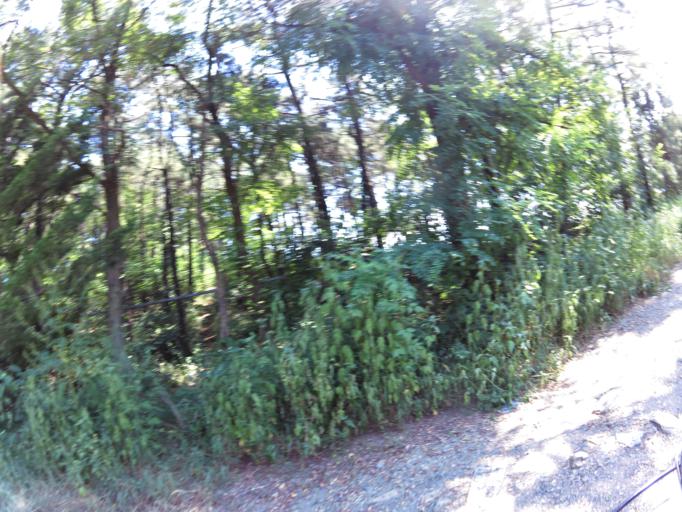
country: KR
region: Daegu
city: Daegu
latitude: 35.8513
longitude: 128.6485
